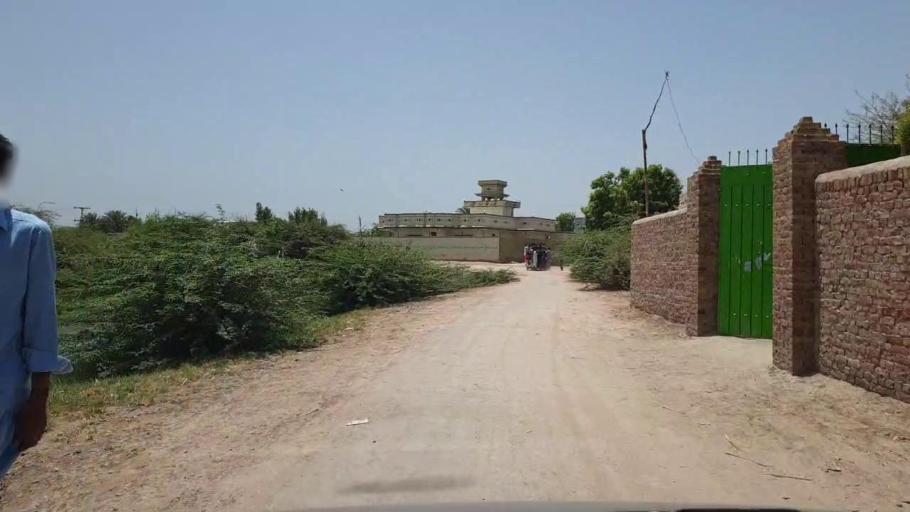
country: PK
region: Sindh
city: Sakrand
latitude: 26.1084
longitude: 68.3902
